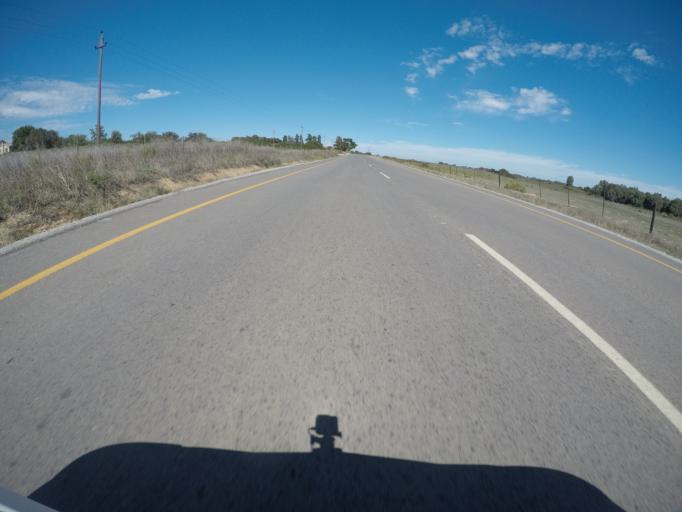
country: ZA
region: Western Cape
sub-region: West Coast District Municipality
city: Malmesbury
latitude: -33.5843
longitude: 18.6468
